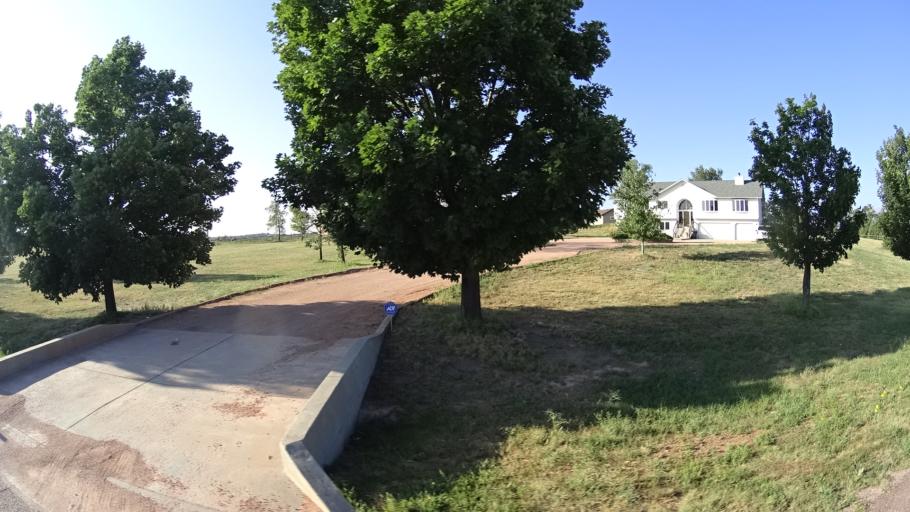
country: US
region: Colorado
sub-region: El Paso County
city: Black Forest
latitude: 38.9402
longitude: -104.7698
